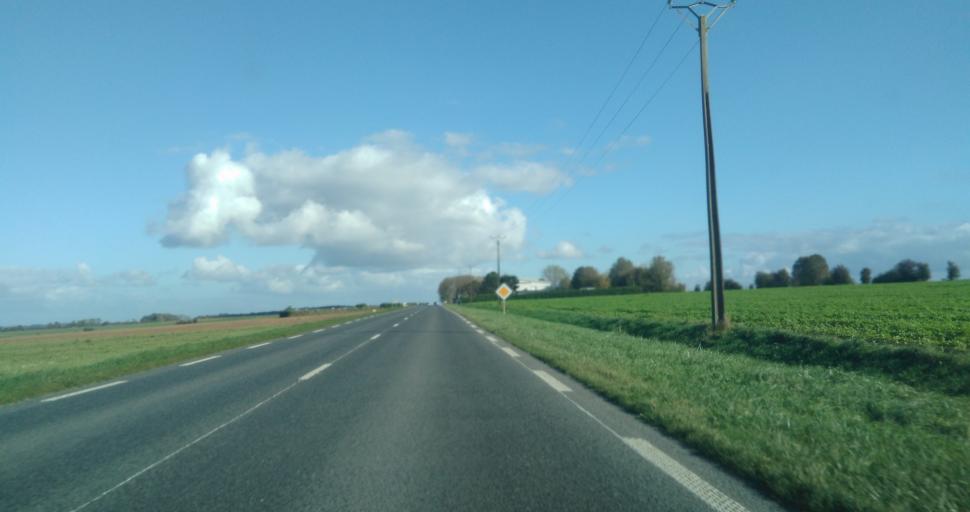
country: FR
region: Nord-Pas-de-Calais
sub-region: Departement du Pas-de-Calais
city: Beaumetz-les-Loges
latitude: 50.2246
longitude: 2.6037
